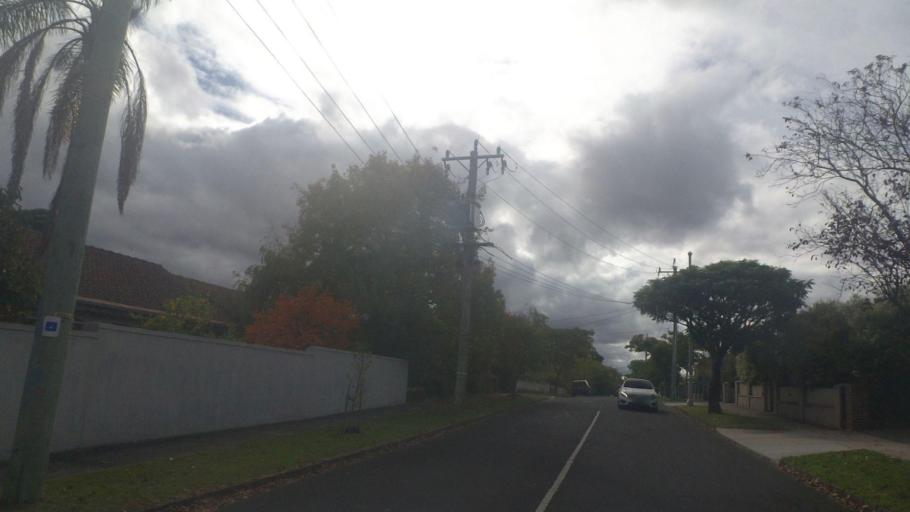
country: AU
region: Victoria
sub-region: Whitehorse
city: Surrey Hills
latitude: -37.8242
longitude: 145.1074
